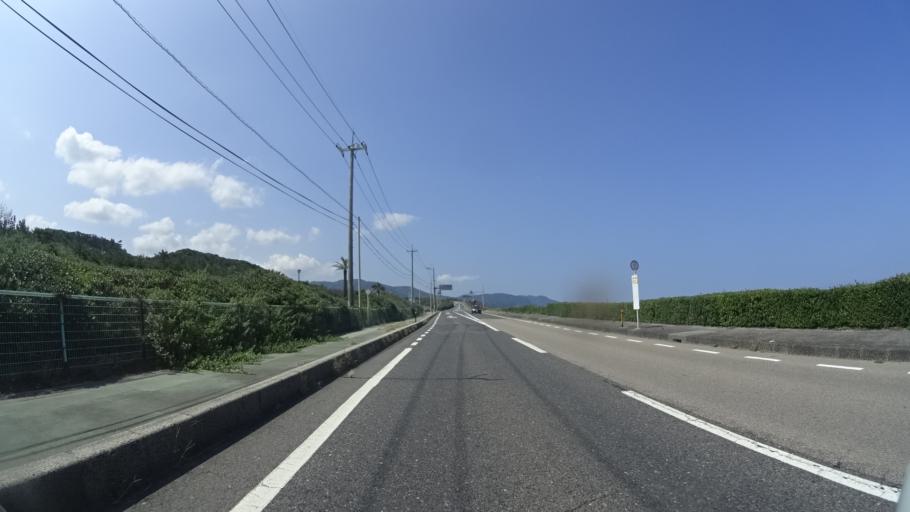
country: JP
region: Shimane
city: Masuda
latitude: 34.6779
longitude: 131.7605
